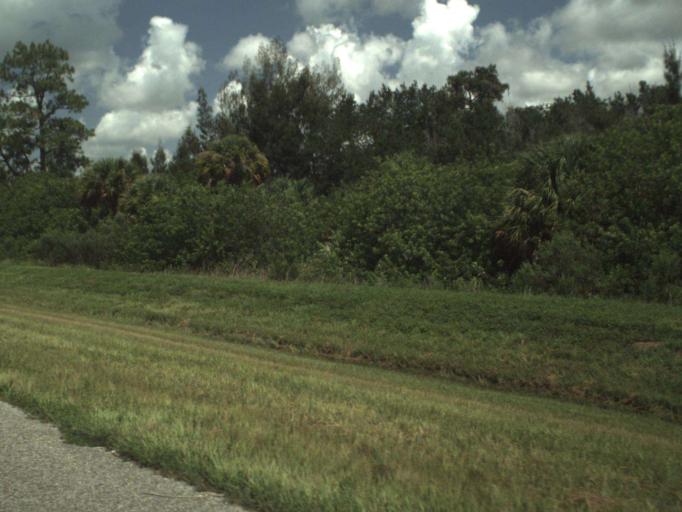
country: US
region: Florida
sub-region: Indian River County
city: West Vero Corridor
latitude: 27.6397
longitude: -80.5541
